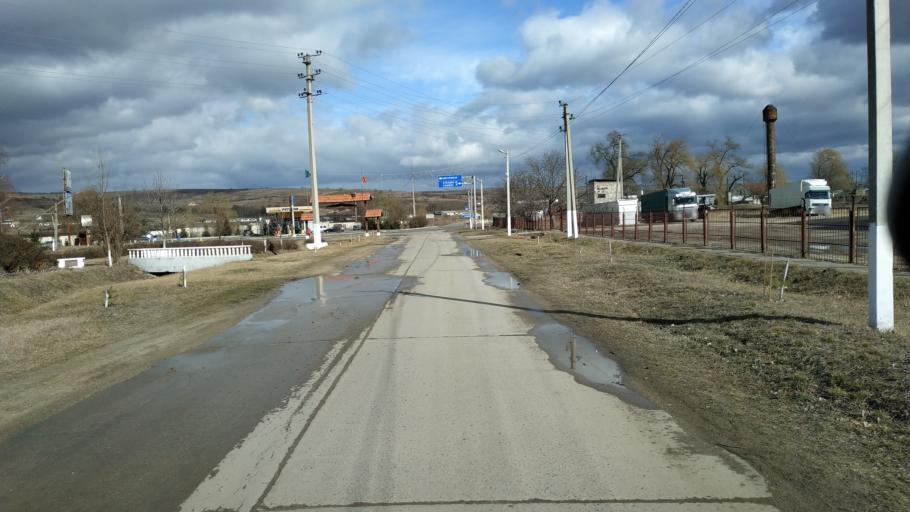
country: MD
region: Stinga Nistrului
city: Bucovat
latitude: 47.1434
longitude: 28.3899
